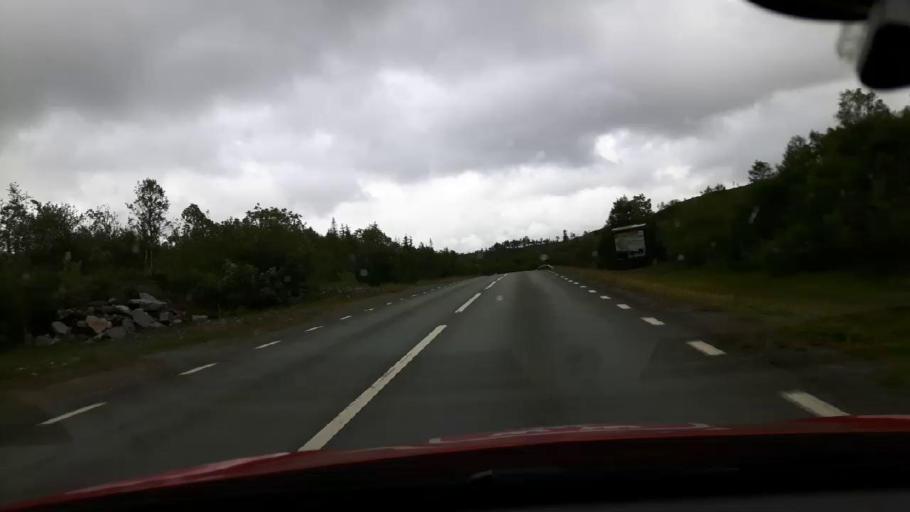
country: NO
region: Nord-Trondelag
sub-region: Meraker
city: Meraker
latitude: 63.3233
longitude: 12.0677
